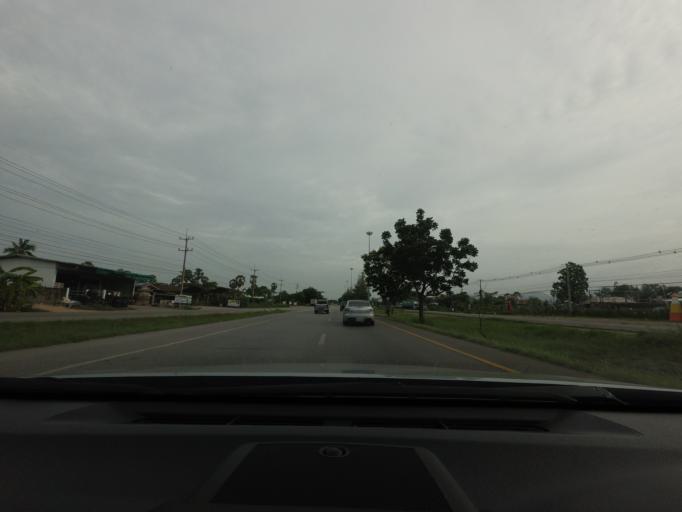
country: TH
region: Phetchaburi
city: Cha-am
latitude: 12.8039
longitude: 99.9426
